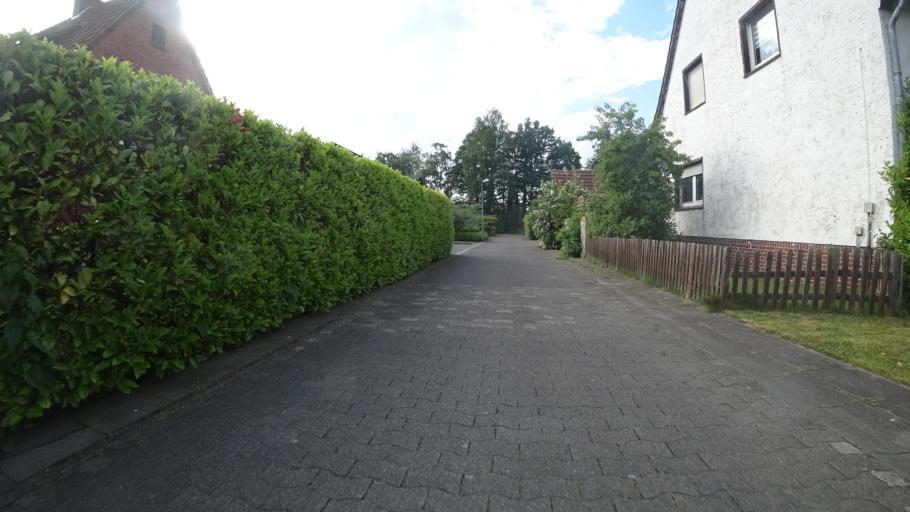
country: DE
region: North Rhine-Westphalia
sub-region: Regierungsbezirk Detmold
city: Guetersloh
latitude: 51.8747
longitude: 8.4291
